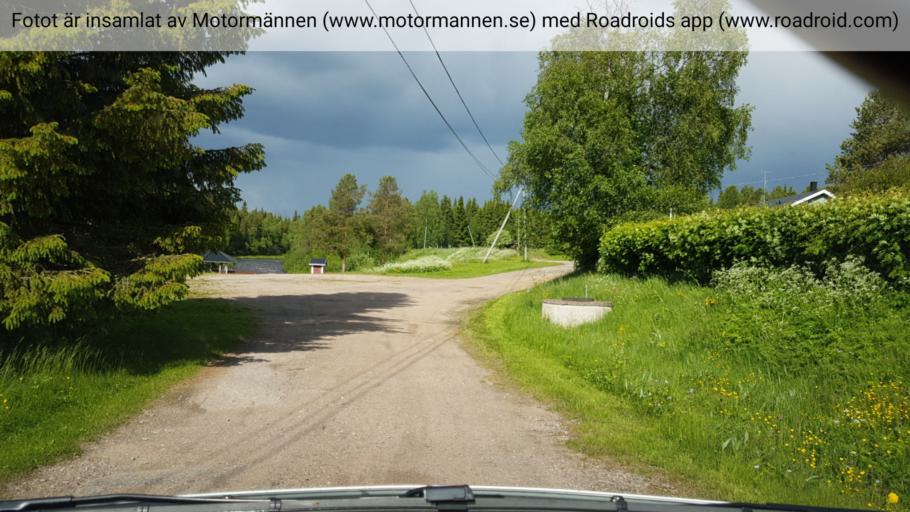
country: FI
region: Lapland
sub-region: Torniolaakso
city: Pello
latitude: 66.8034
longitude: 23.8997
